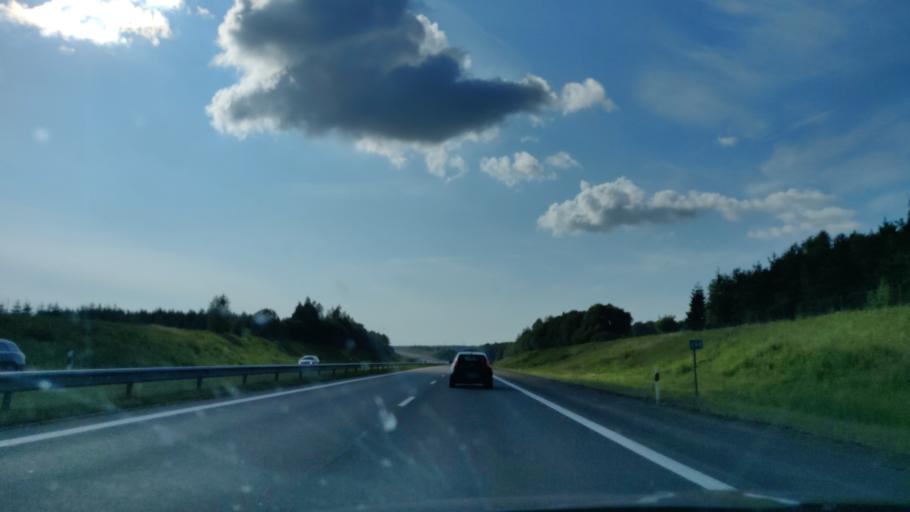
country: LT
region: Klaipedos apskritis
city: Gargzdai
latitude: 55.7236
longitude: 21.4278
